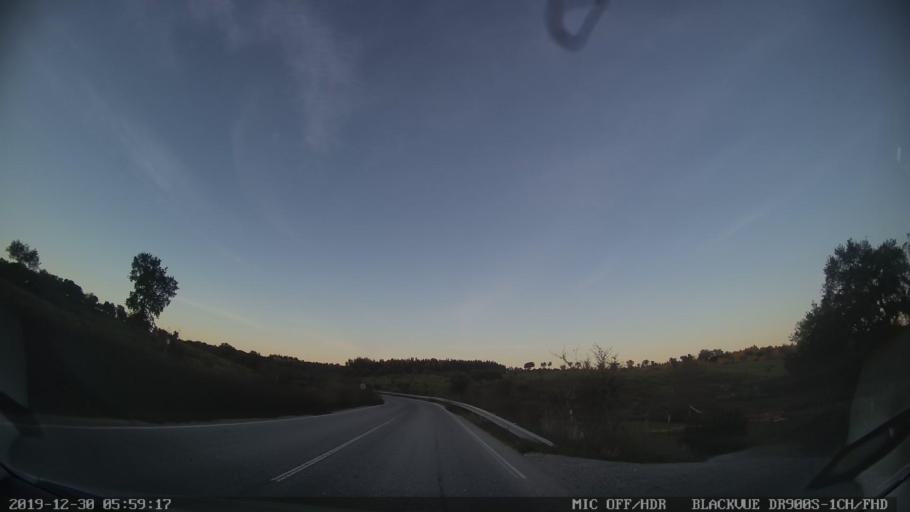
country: PT
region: Castelo Branco
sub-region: Idanha-A-Nova
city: Idanha-a-Nova
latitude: 40.0428
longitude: -7.2424
